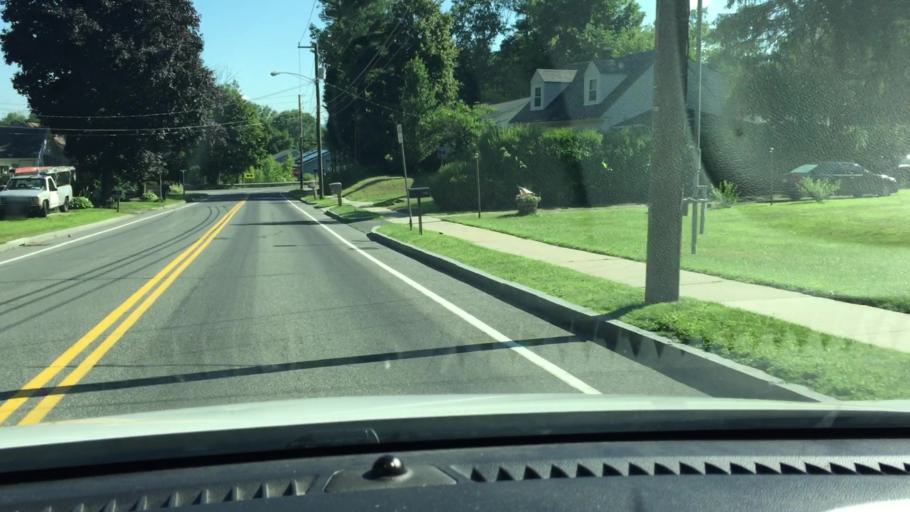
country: US
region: Massachusetts
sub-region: Berkshire County
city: Pittsfield
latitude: 42.4864
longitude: -73.2591
